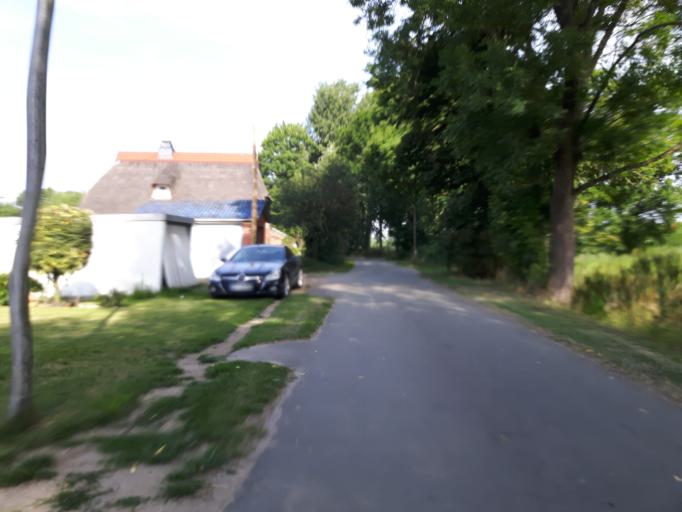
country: DE
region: Lower Saxony
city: Lemwerder
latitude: 53.1485
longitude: 8.5603
